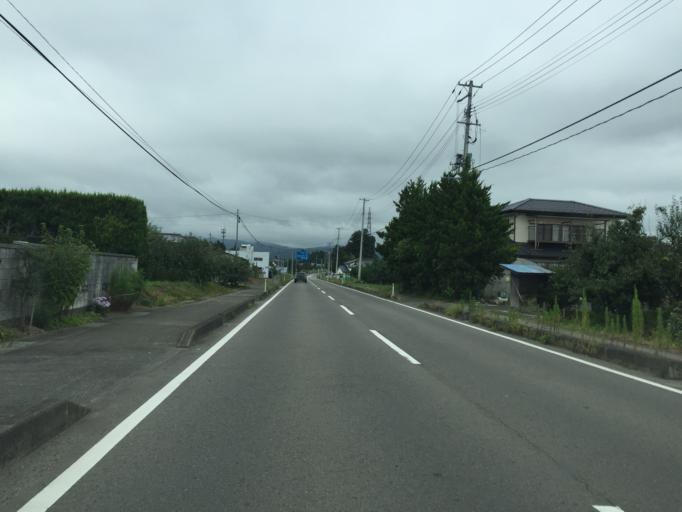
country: JP
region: Fukushima
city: Fukushima-shi
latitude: 37.7515
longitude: 140.4020
